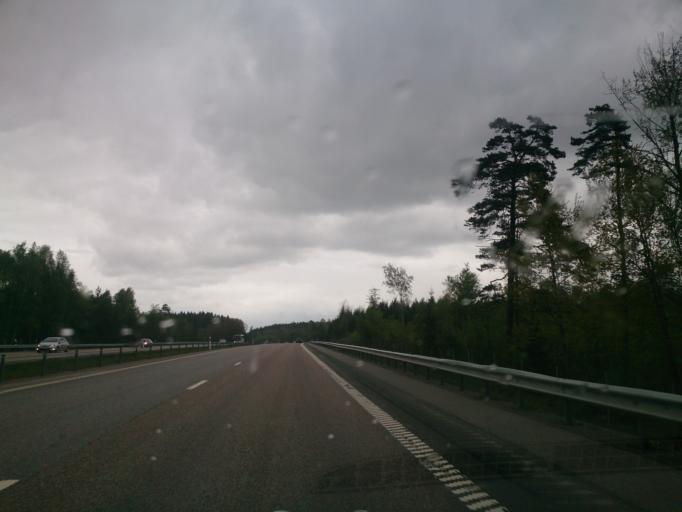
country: SE
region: Soedermanland
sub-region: Trosa Kommun
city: Vagnharad
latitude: 59.0545
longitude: 17.5730
